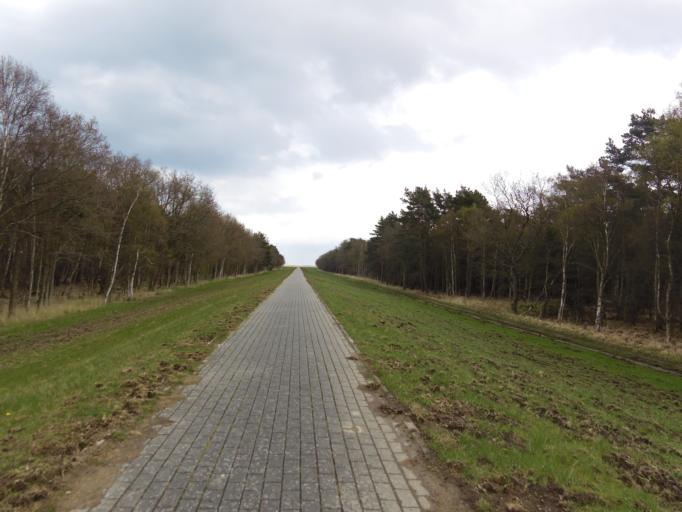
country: DE
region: Mecklenburg-Vorpommern
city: Zingst
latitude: 54.4408
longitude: 12.7623
